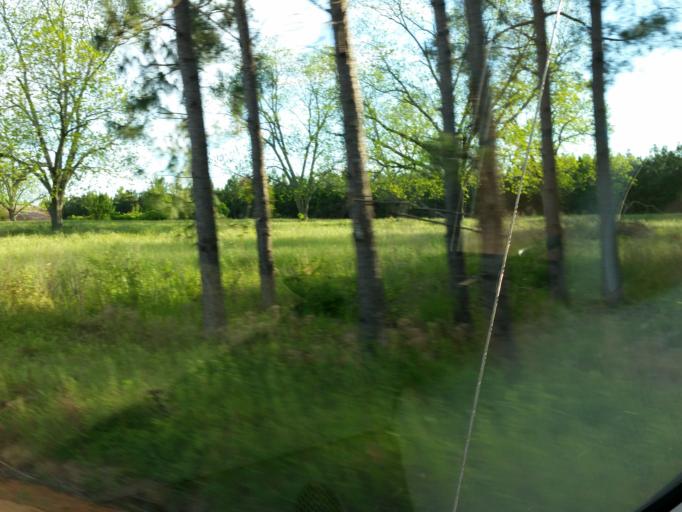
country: US
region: Georgia
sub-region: Turner County
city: Ashburn
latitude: 31.6574
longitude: -83.6309
